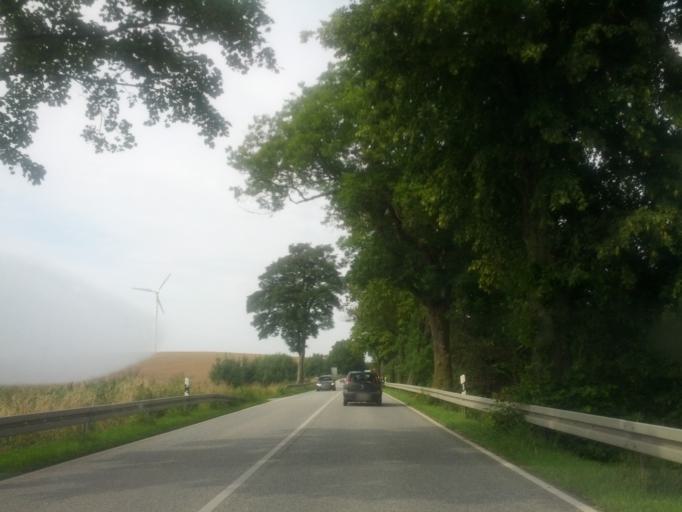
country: DE
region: Mecklenburg-Vorpommern
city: Neubukow
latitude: 53.9820
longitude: 11.6271
